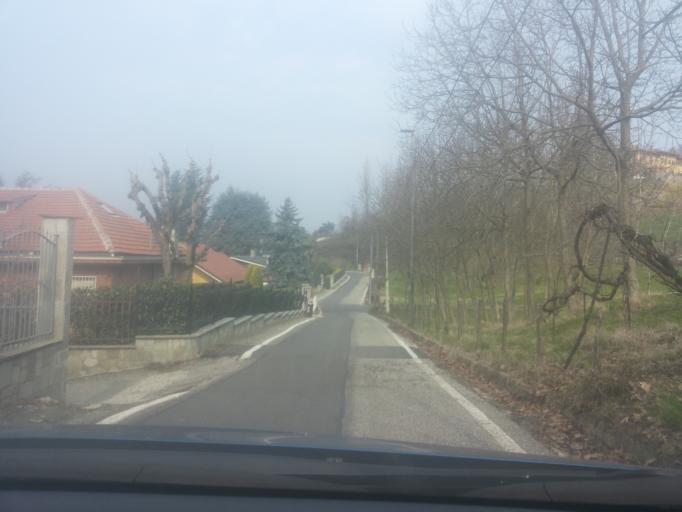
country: IT
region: Piedmont
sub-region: Provincia di Torino
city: Revigliasco
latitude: 45.0535
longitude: 7.7291
